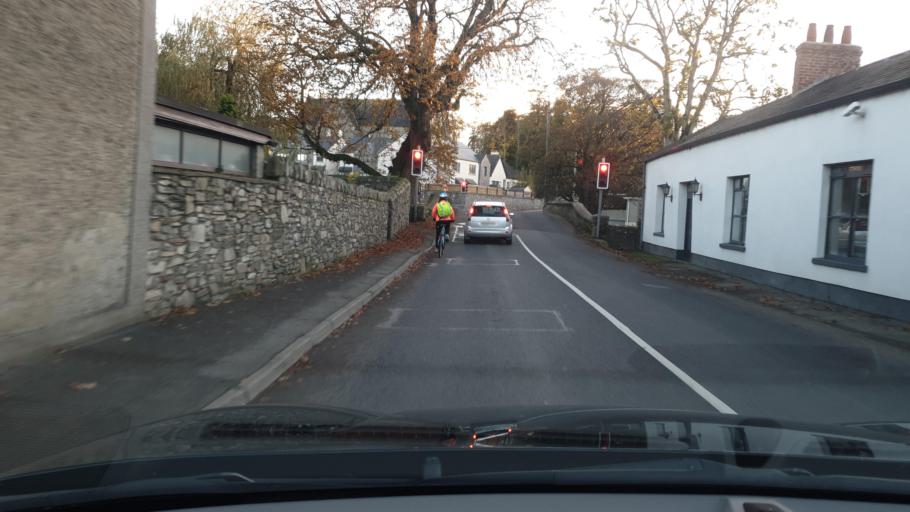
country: IE
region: Leinster
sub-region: Lu
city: Termonfeckin
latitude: 53.7606
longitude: -6.2719
